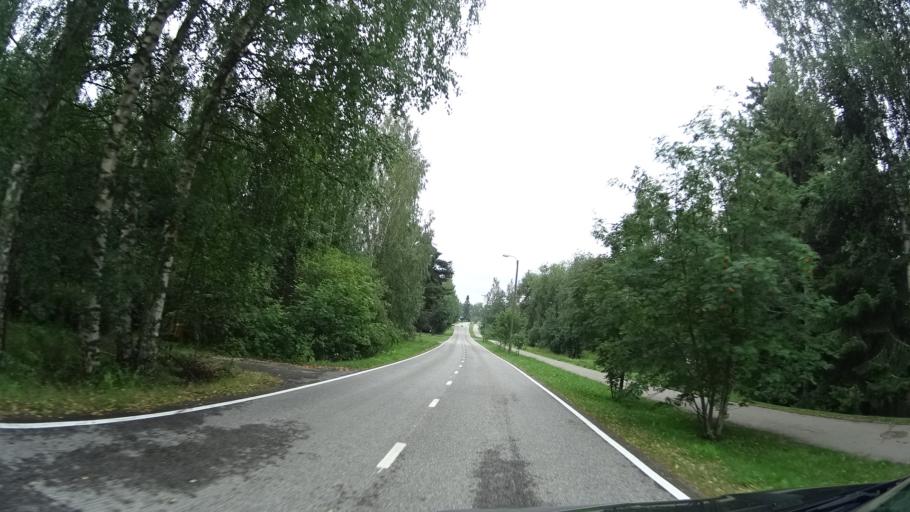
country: FI
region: Southern Savonia
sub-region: Savonlinna
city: Punkaharju
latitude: 61.7503
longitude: 29.3906
